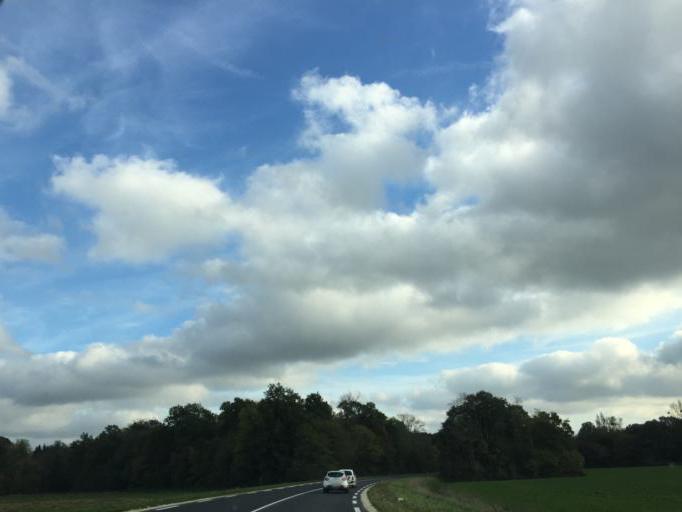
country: FR
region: Ile-de-France
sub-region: Departement de Seine-et-Marne
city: Villeneuve-le-Comte
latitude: 48.8219
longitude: 2.8406
